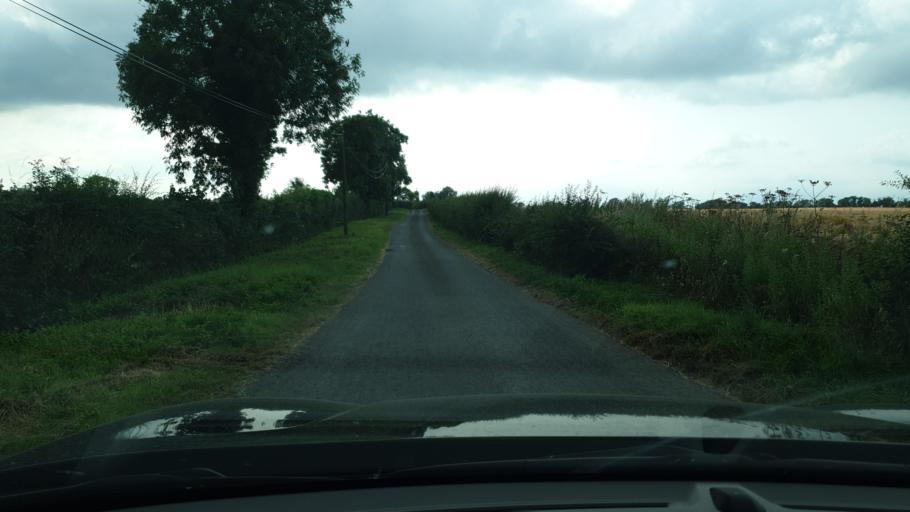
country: IE
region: Leinster
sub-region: An Mhi
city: Ratoath
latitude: 53.4733
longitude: -6.4422
